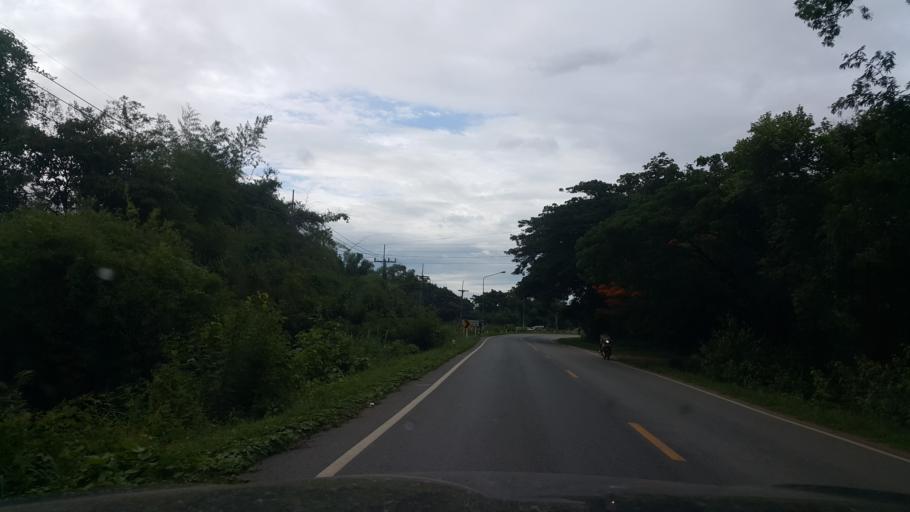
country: TH
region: Sukhothai
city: Ban Na
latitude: 17.0343
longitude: 99.7030
